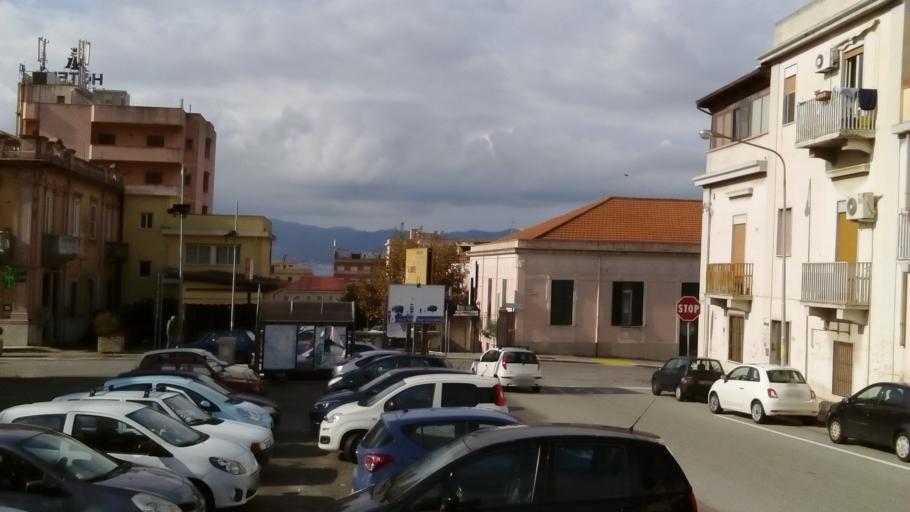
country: IT
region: Calabria
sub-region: Provincia di Reggio Calabria
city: Campo Calabro
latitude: 38.2164
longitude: 15.6388
